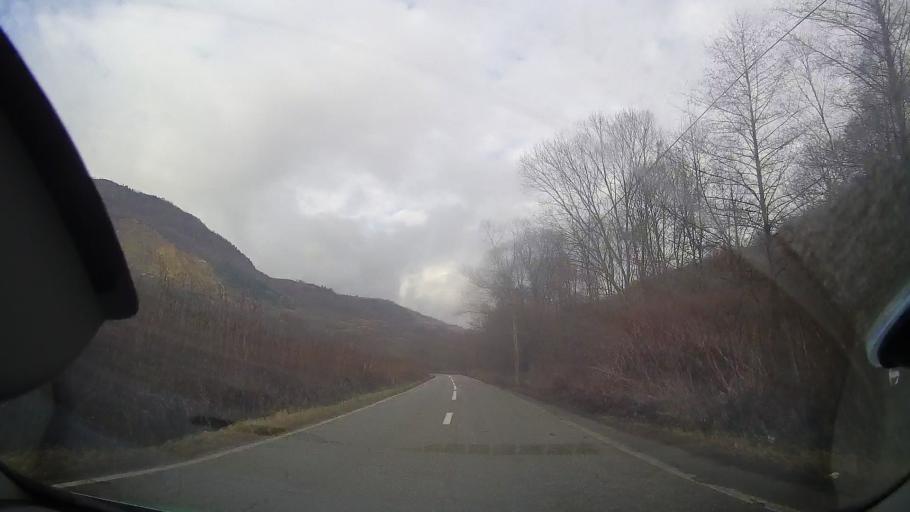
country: RO
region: Alba
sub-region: Comuna Ocolis
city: Ocolis
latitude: 46.4494
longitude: 23.4693
